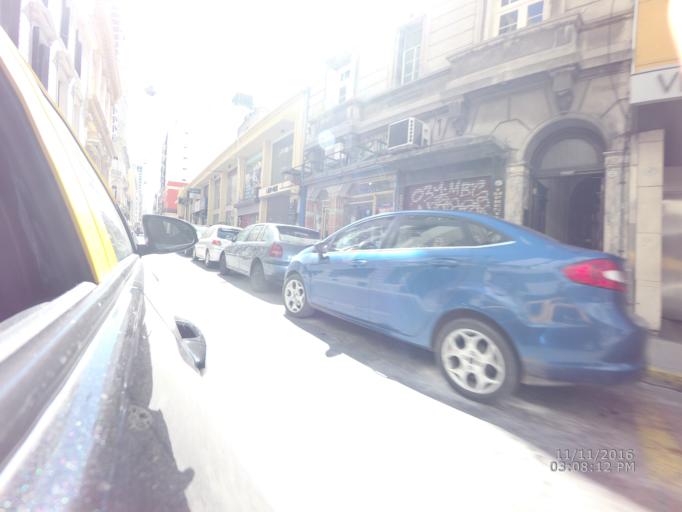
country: AR
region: Buenos Aires F.D.
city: Buenos Aires
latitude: -34.6009
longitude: -58.3733
